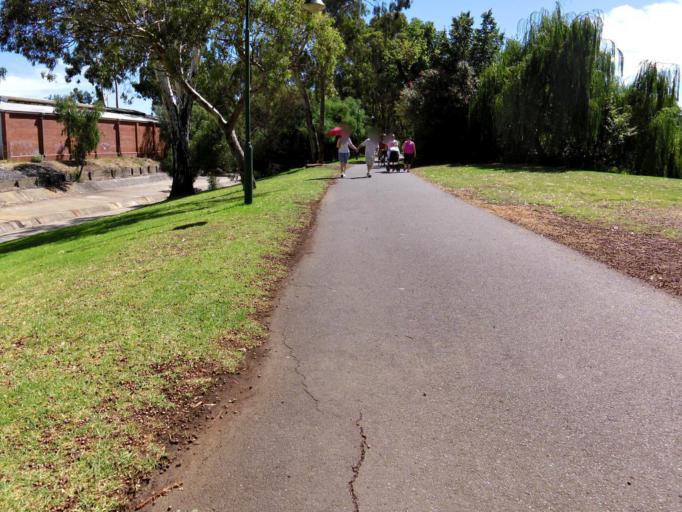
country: AU
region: Victoria
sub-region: Greater Bendigo
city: Bendigo
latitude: -36.7451
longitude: 144.2914
